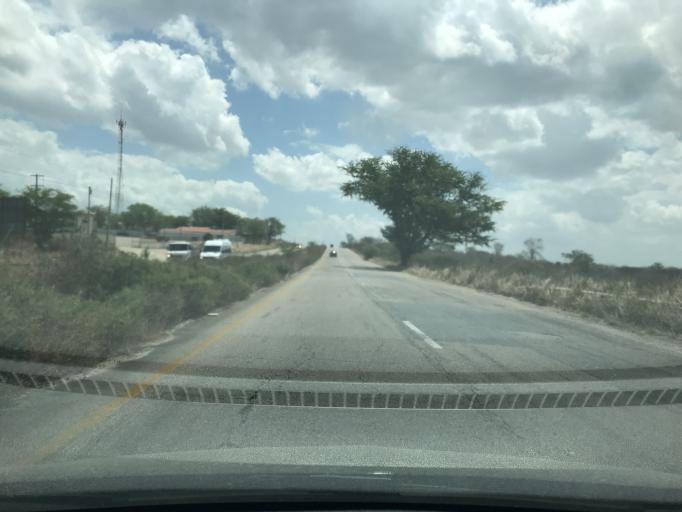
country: BR
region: Pernambuco
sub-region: Caruaru
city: Caruaru
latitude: -8.2979
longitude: -35.8997
